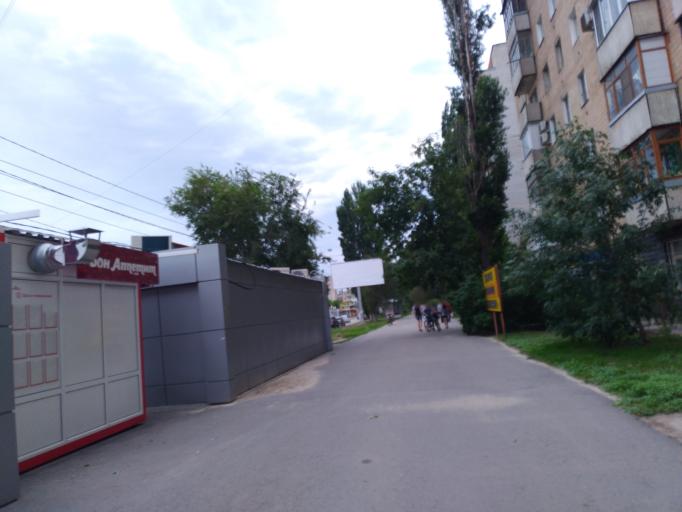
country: RU
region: Volgograd
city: Volgograd
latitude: 48.7234
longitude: 44.5148
